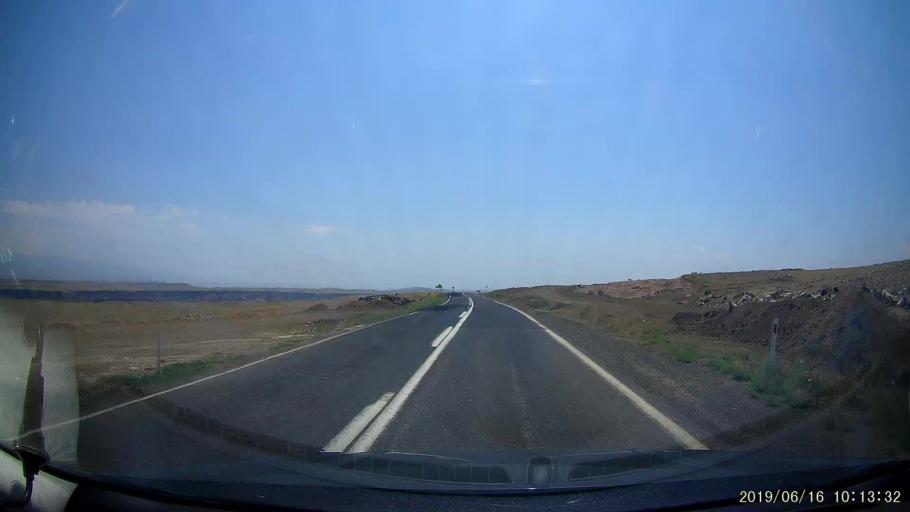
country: TR
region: Igdir
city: Tuzluca
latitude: 40.1921
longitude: 43.6448
